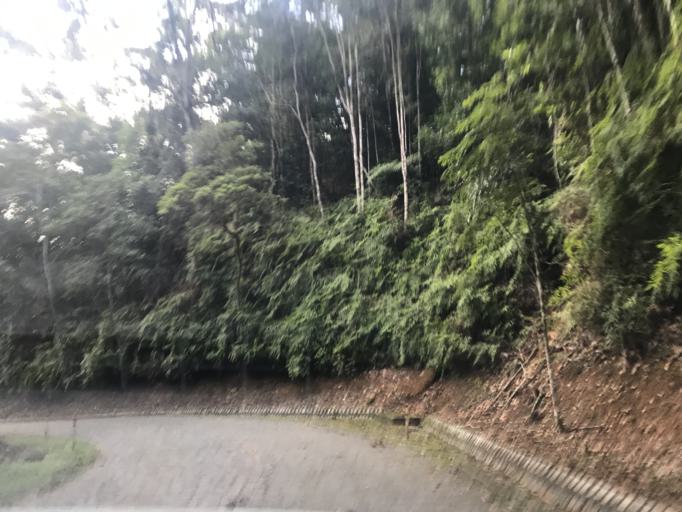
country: BR
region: Bahia
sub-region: Gandu
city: Gandu
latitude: -13.9099
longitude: -39.4646
